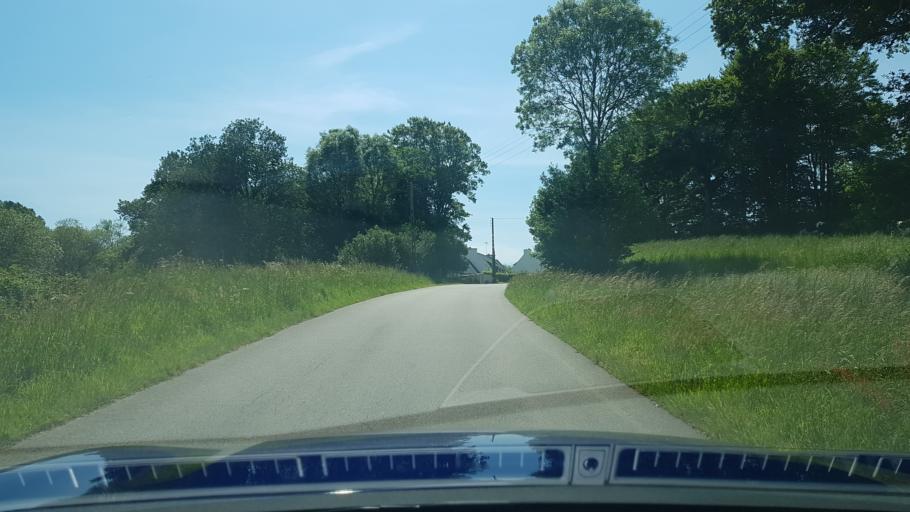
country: FR
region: Brittany
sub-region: Departement du Finistere
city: Clohars-Carnoet
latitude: 47.7885
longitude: -3.5534
